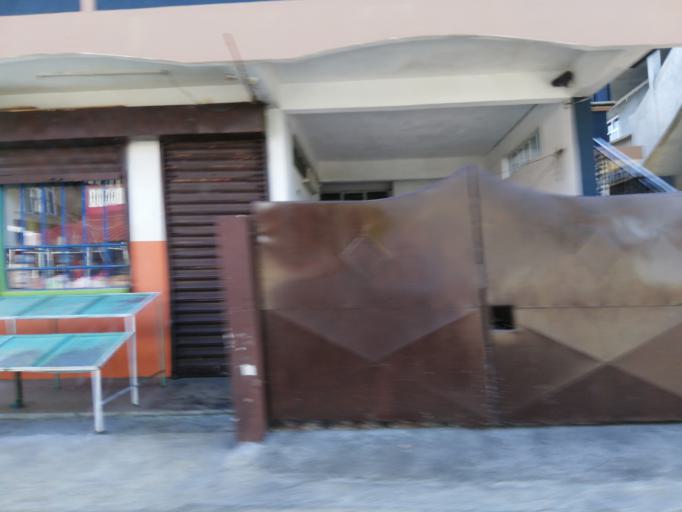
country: MU
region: Moka
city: Verdun
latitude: -20.2203
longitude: 57.5352
